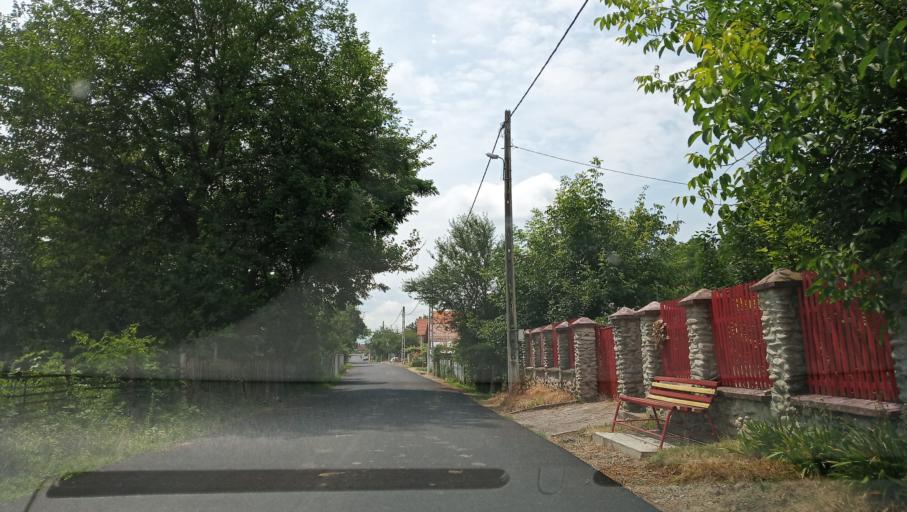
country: RO
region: Gorj
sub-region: Comuna Turcinesti
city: Turcinesti
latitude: 45.1407
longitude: 23.3421
